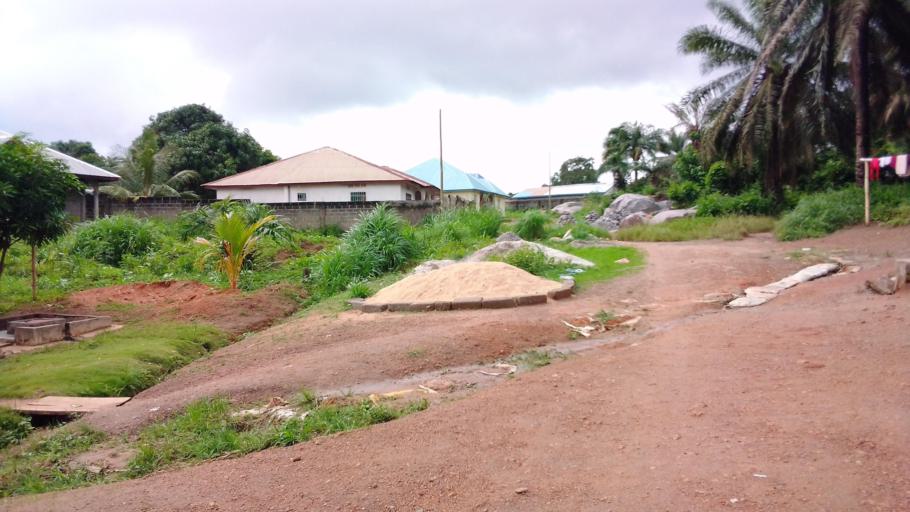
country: SL
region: Eastern Province
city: Kenema
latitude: 7.8710
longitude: -11.1749
